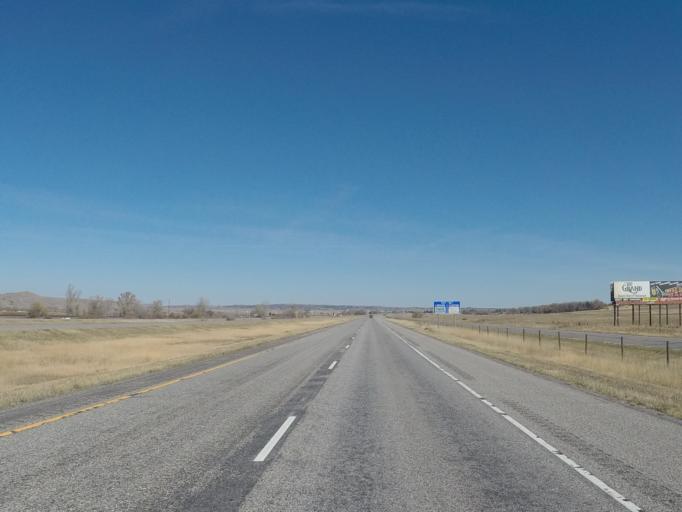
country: US
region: Montana
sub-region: Sweet Grass County
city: Big Timber
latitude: 45.8198
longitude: -109.9878
